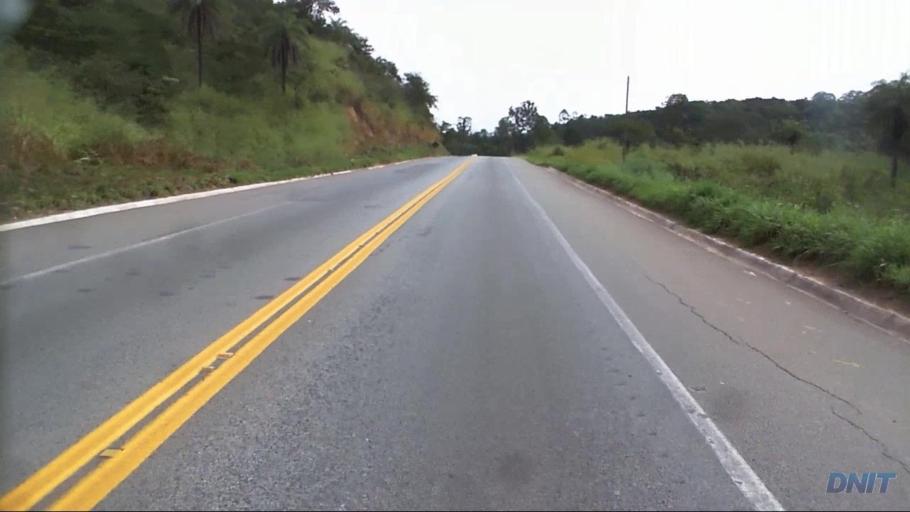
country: BR
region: Minas Gerais
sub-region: Santa Luzia
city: Santa Luzia
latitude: -19.8288
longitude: -43.8409
